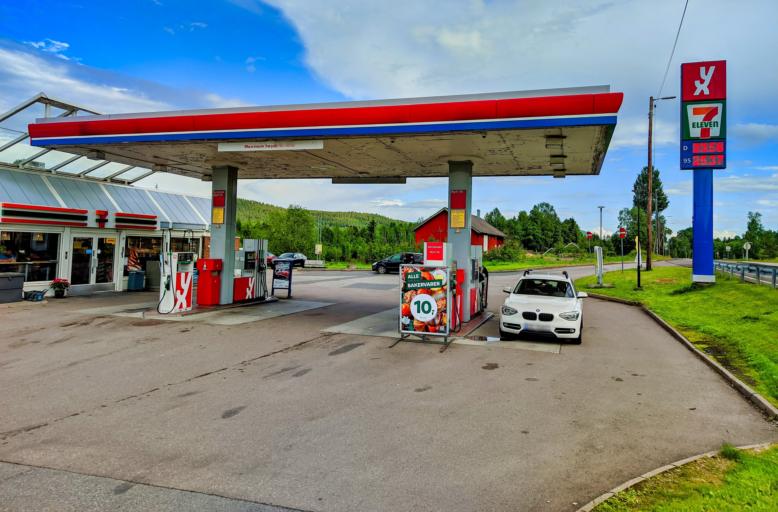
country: NO
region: Akershus
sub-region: Nittedal
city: Aneby
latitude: 60.1006
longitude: 10.8658
